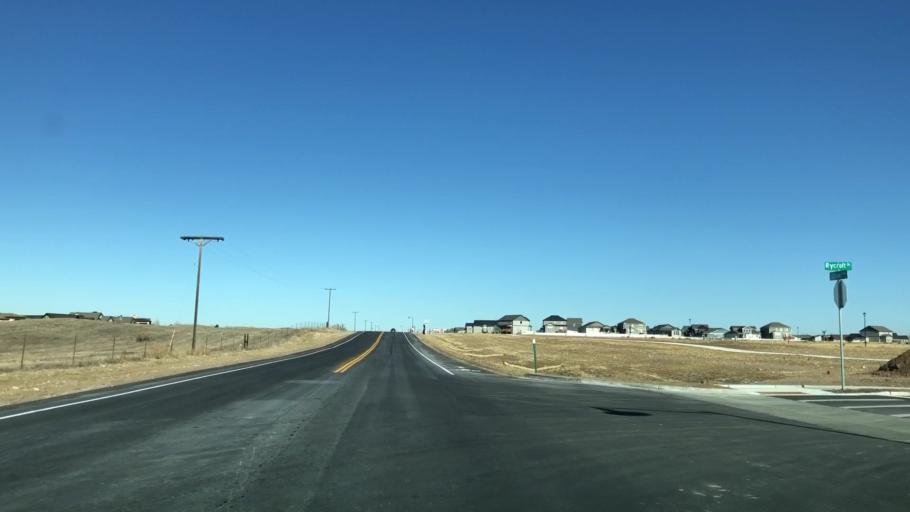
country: US
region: Colorado
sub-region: Weld County
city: Windsor
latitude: 40.5264
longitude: -104.9442
